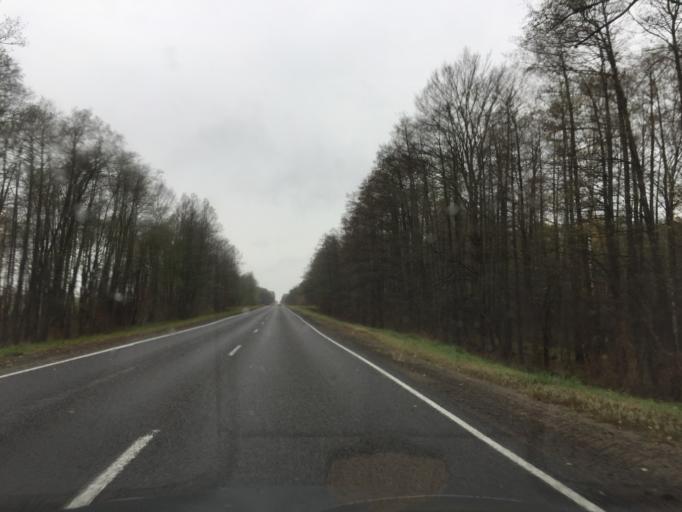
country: BY
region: Mogilev
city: Slawharad
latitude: 53.3534
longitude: 30.8277
